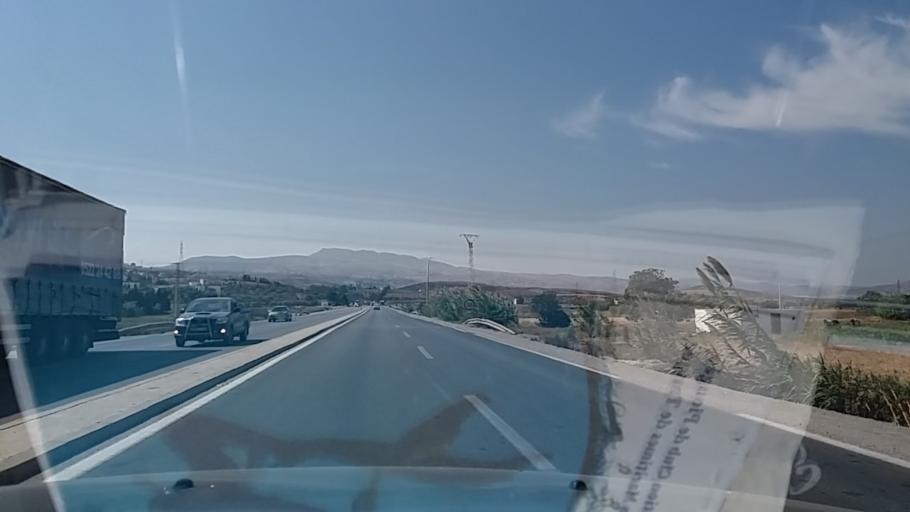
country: MA
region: Tanger-Tetouan
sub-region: Tetouan
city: Saddina
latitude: 35.5595
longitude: -5.4625
